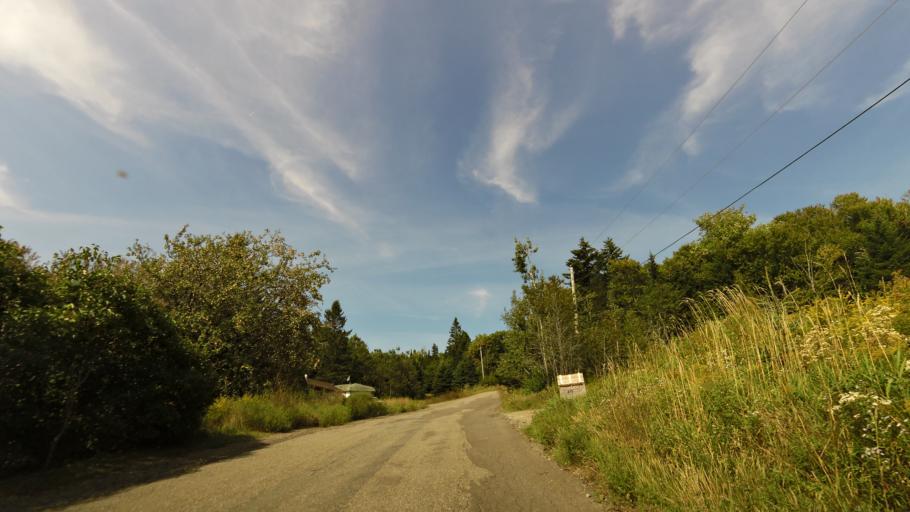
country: CA
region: New Brunswick
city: Hampton
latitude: 45.5606
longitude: -65.8441
